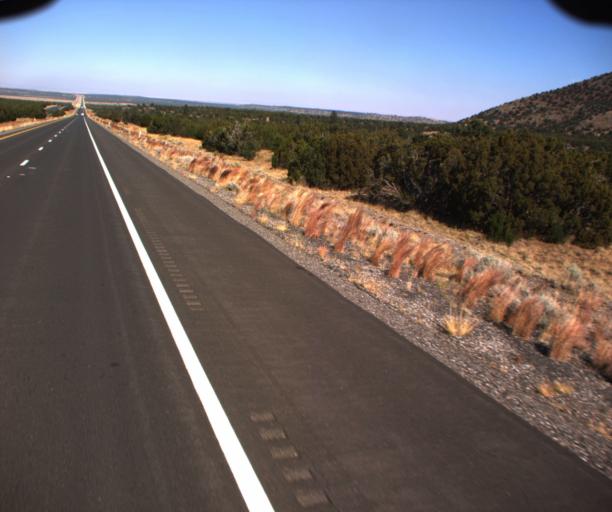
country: US
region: Arizona
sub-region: Coconino County
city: Flagstaff
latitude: 35.4079
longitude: -111.5739
